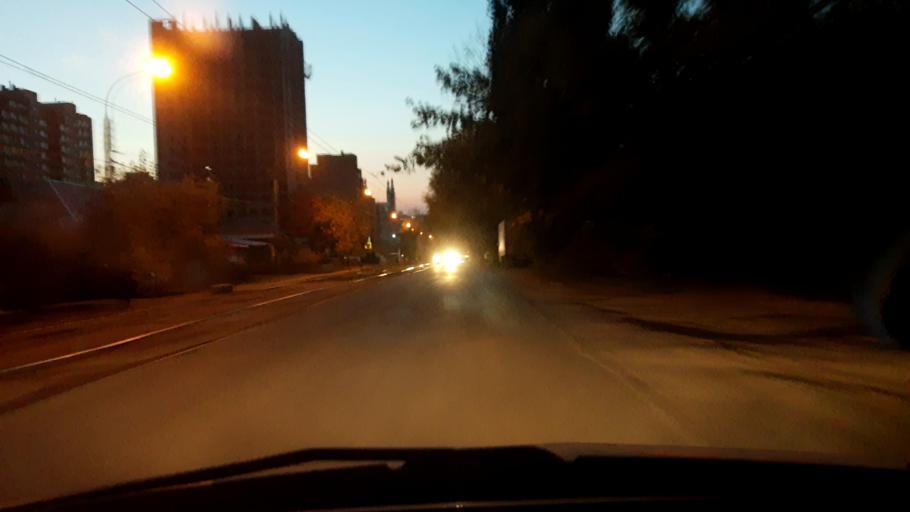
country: RU
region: Bashkortostan
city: Ufa
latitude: 54.7137
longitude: 55.9789
